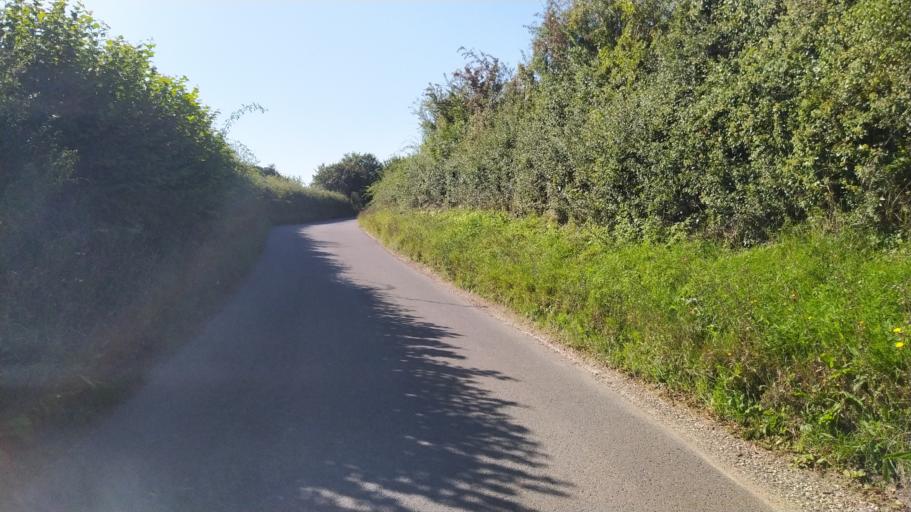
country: GB
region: England
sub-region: Hampshire
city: Abbotts Ann
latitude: 51.1719
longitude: -1.6049
